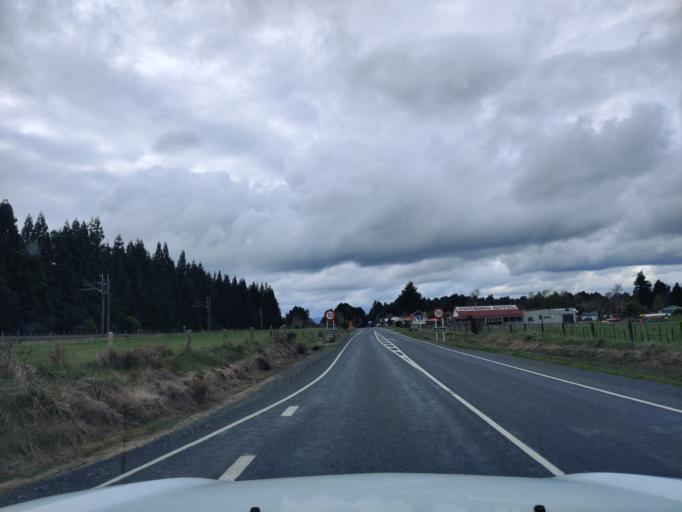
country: NZ
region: Waikato
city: Turangi
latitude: -39.0024
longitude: 175.3768
